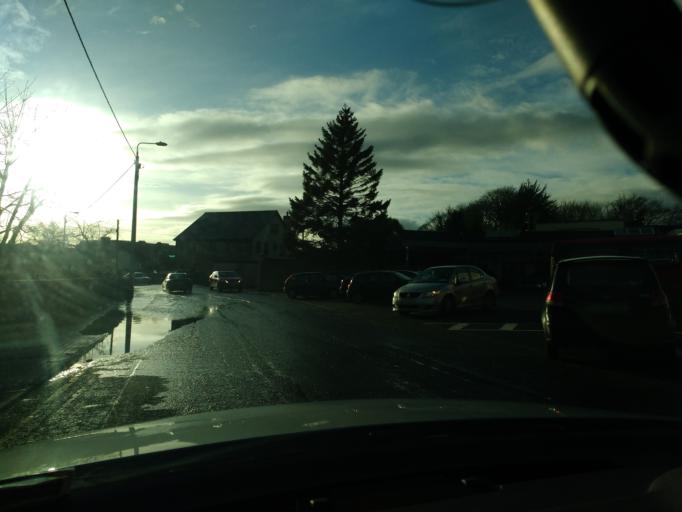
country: IE
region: Munster
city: Thurles
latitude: 52.6785
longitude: -7.8107
